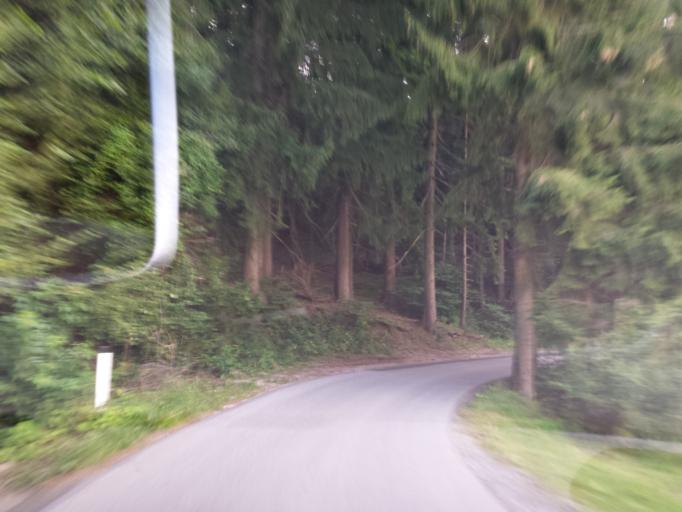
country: AT
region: Styria
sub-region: Politischer Bezirk Graz-Umgebung
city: Stattegg
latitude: 47.1511
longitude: 15.4452
